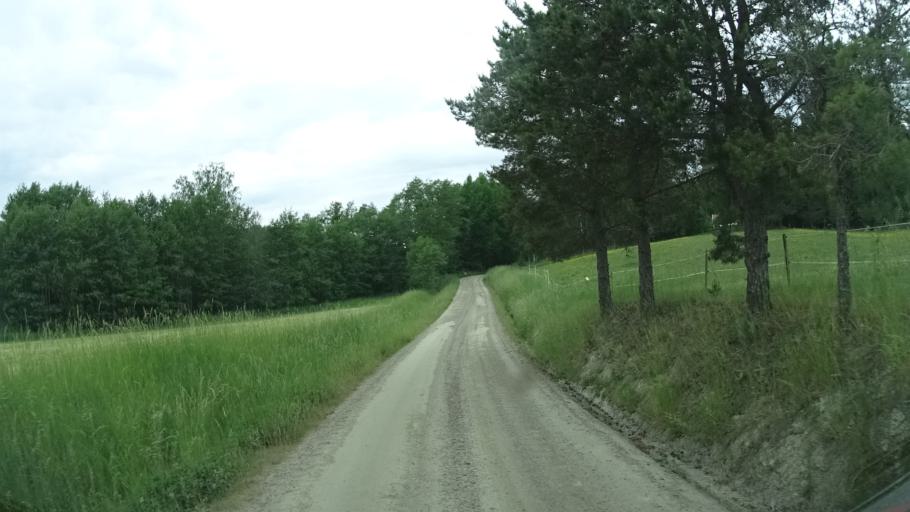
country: SE
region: Soedermanland
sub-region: Nykopings Kommun
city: Olstorp
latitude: 58.7638
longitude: 16.6965
